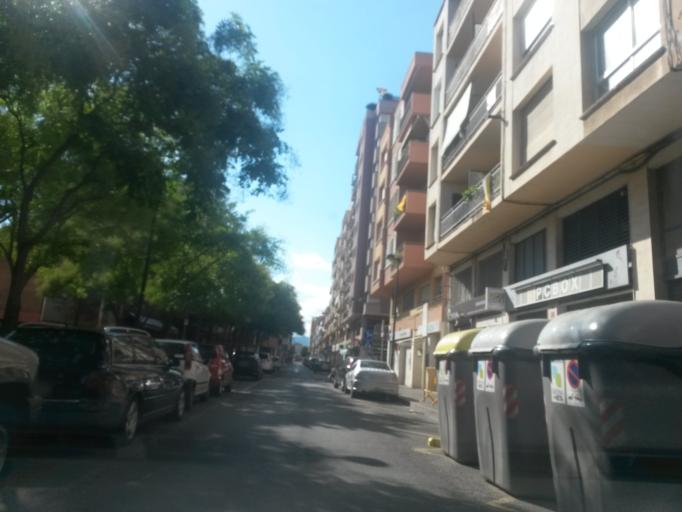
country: ES
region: Catalonia
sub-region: Provincia de Girona
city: Girona
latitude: 41.9693
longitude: 2.8178
